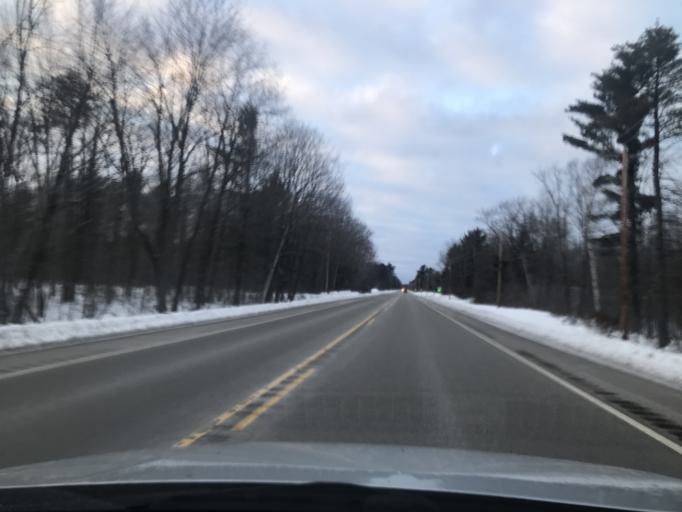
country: US
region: Wisconsin
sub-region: Marinette County
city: Marinette
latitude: 45.1411
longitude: -87.6924
